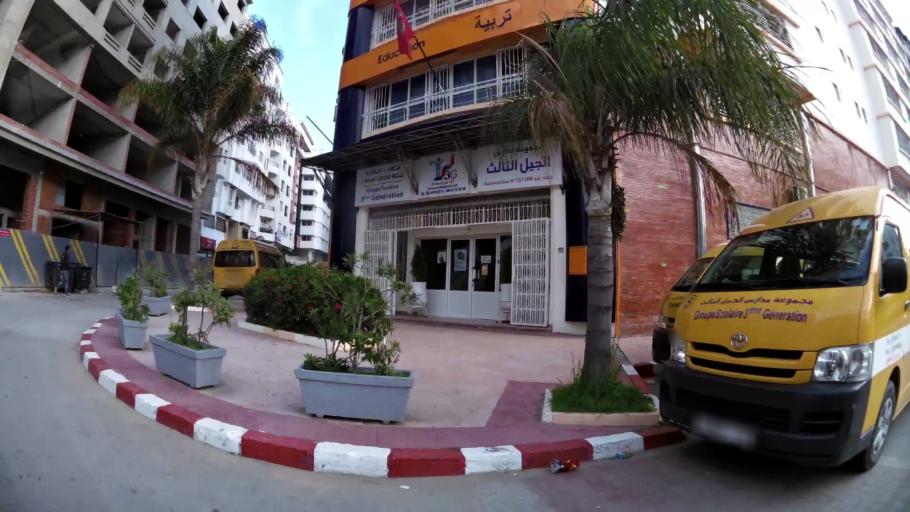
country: MA
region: Tanger-Tetouan
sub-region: Tanger-Assilah
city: Tangier
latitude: 35.7727
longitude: -5.7999
